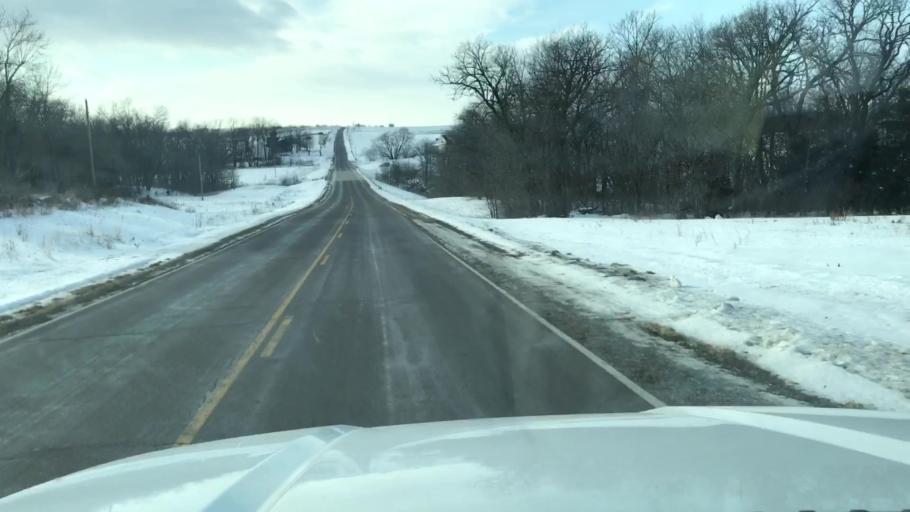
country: US
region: Missouri
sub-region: Nodaway County
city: Maryville
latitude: 40.2007
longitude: -94.8914
